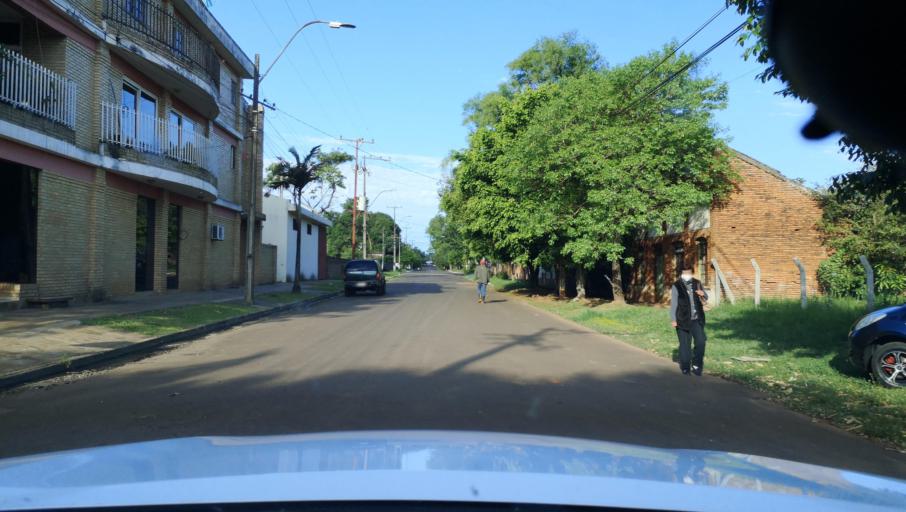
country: PY
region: Itapua
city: Carmen del Parana
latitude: -27.1601
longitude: -56.2379
